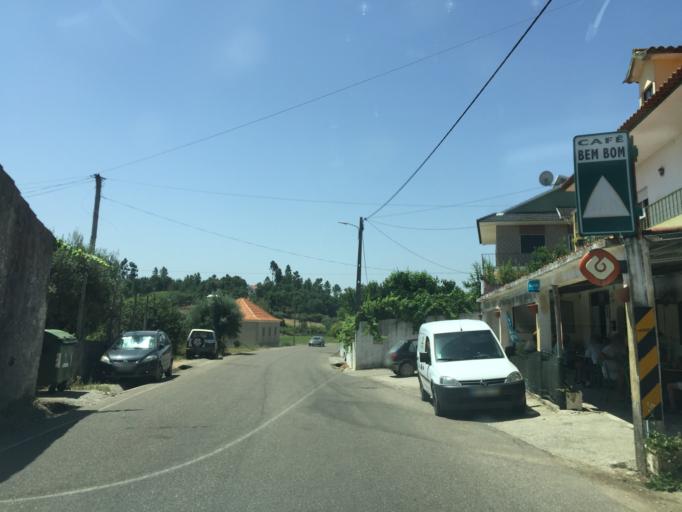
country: PT
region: Santarem
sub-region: Ferreira do Zezere
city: Ferreira do Zezere
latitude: 39.6358
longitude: -8.3060
